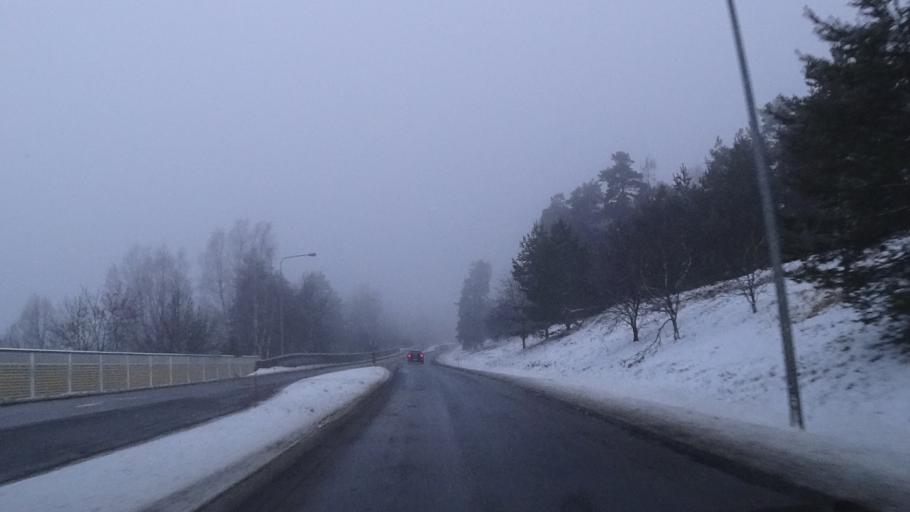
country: FI
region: Paijanne Tavastia
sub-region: Lahti
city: Hollola
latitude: 60.9825
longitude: 25.5434
